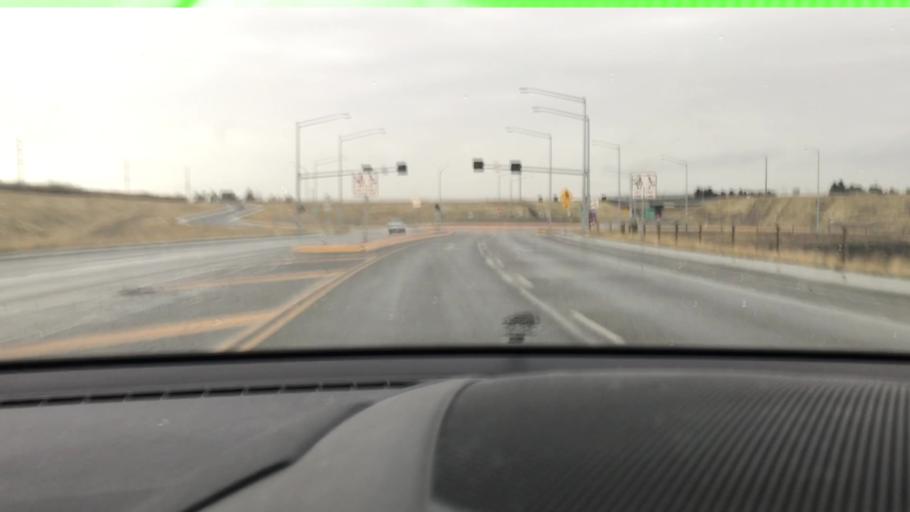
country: US
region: Montana
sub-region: Gallatin County
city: Belgrade
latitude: 45.7647
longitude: -111.1632
